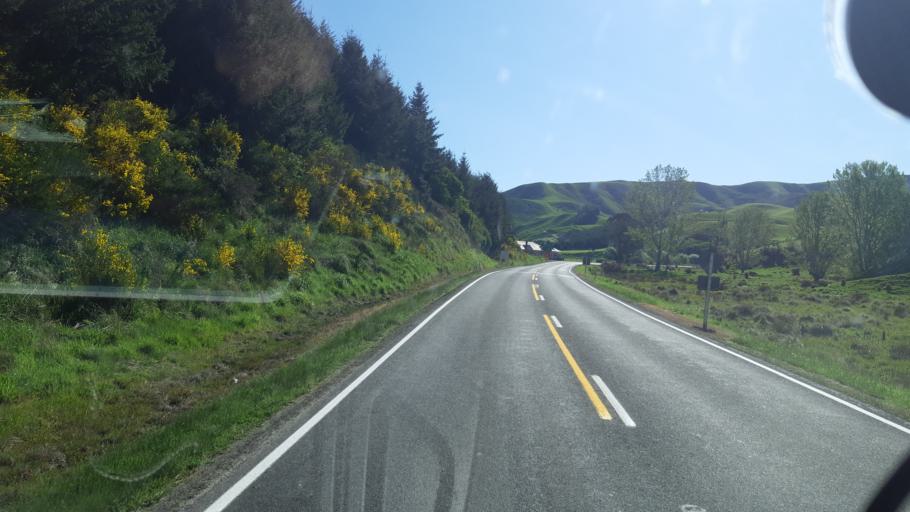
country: NZ
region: Otago
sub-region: Clutha District
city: Balclutha
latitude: -45.7867
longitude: 169.4731
